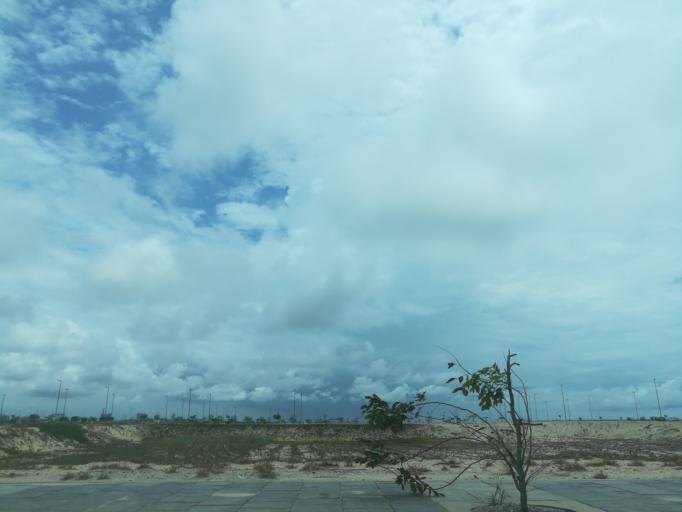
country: NG
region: Lagos
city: Ikoyi
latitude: 6.4061
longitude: 3.4170
